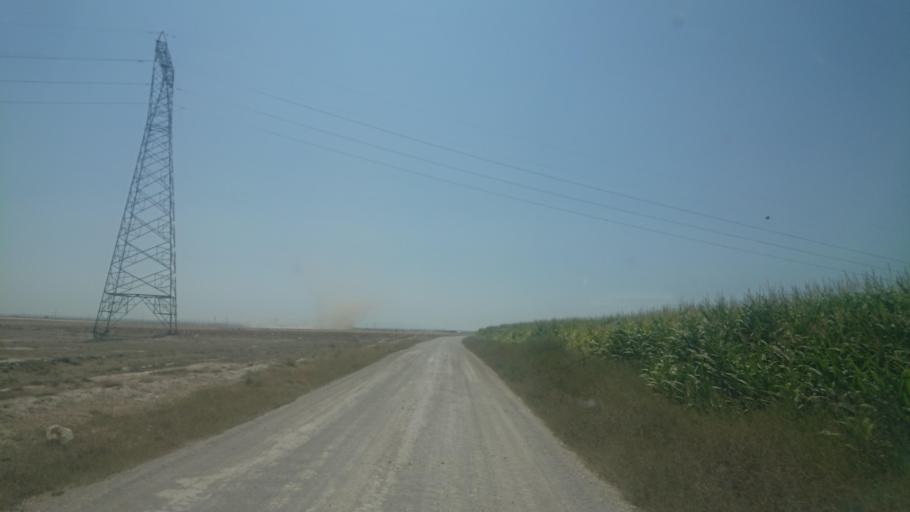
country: TR
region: Aksaray
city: Sultanhani
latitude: 38.2495
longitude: 33.6517
